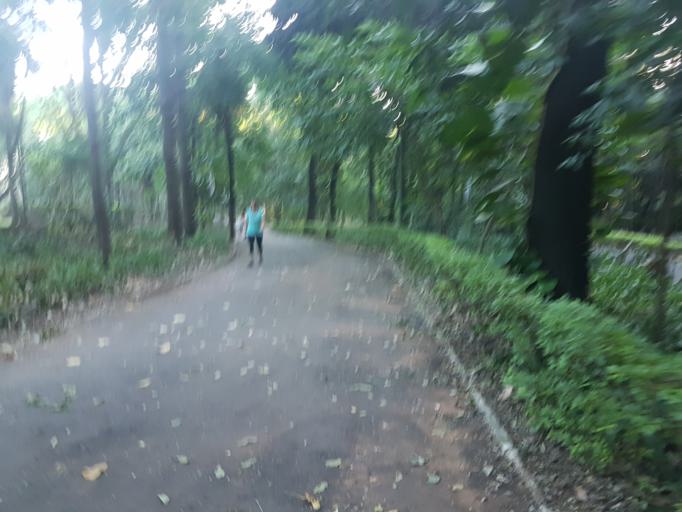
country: PY
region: Asuncion
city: Asuncion
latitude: -25.2771
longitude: -57.5787
